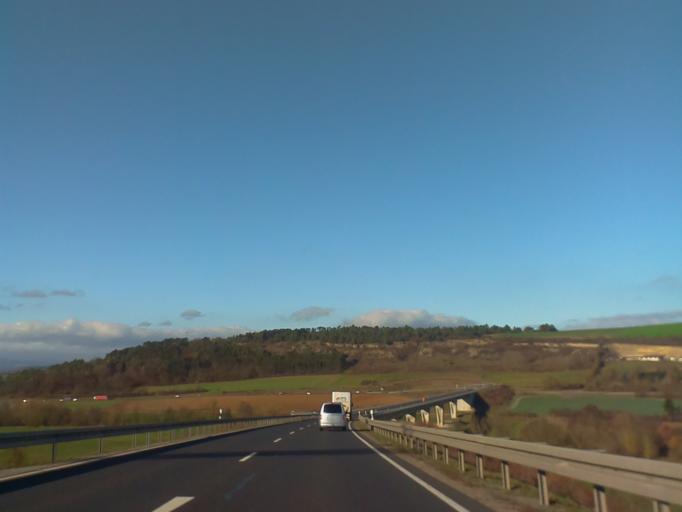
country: DE
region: Bavaria
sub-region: Regierungsbezirk Unterfranken
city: Heustreu
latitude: 50.3347
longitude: 10.2512
